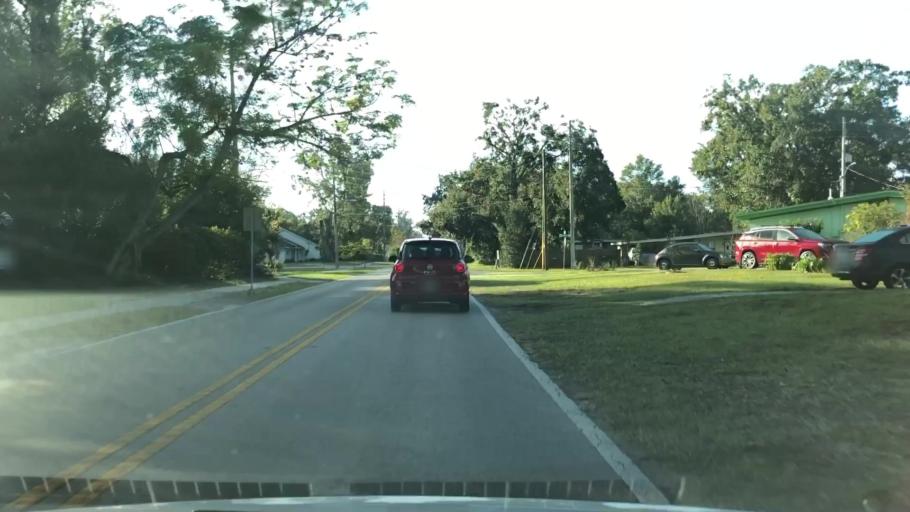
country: US
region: Florida
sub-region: Orange County
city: Conway
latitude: 28.5360
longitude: -81.3436
